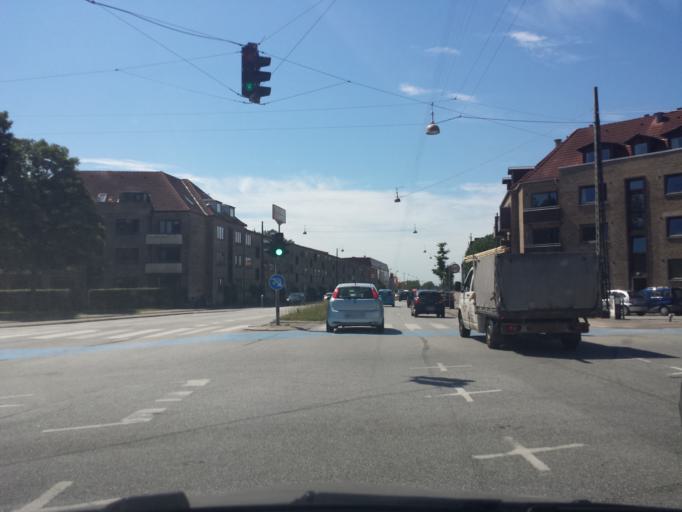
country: DK
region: Capital Region
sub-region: Frederiksberg Kommune
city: Frederiksberg
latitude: 55.6502
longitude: 12.5281
